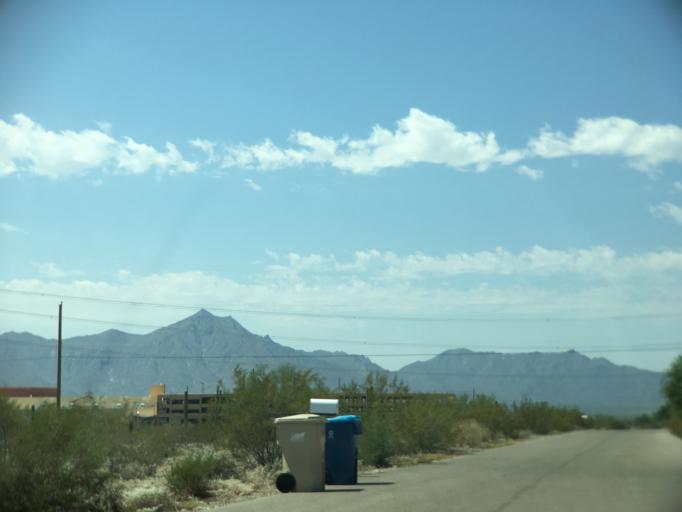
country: US
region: Arizona
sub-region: Maricopa County
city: Laveen
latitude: 33.3122
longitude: -112.1519
